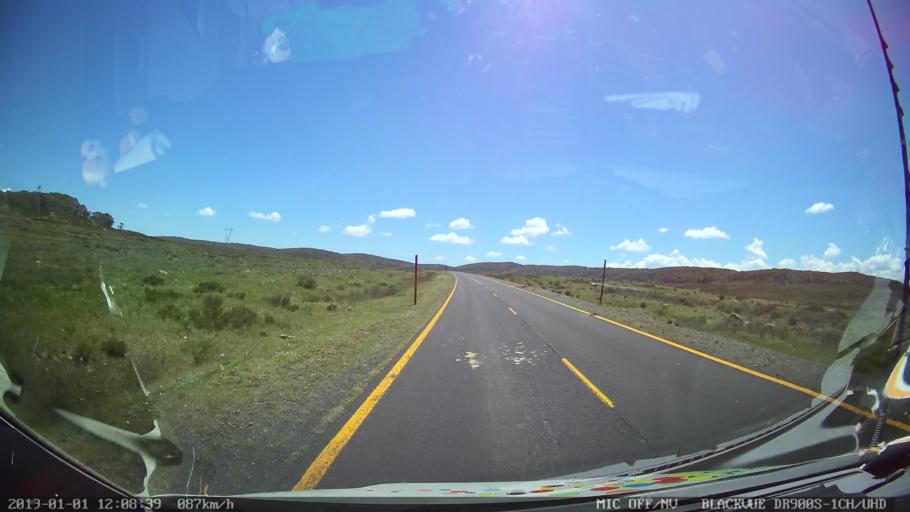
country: AU
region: New South Wales
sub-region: Tumut Shire
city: Tumut
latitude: -35.8176
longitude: 148.4958
